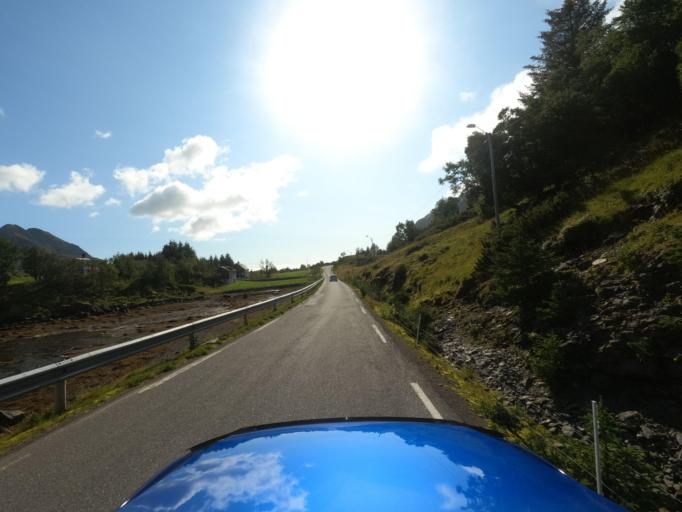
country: NO
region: Nordland
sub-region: Vestvagoy
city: Evjen
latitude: 68.1452
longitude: 13.7469
